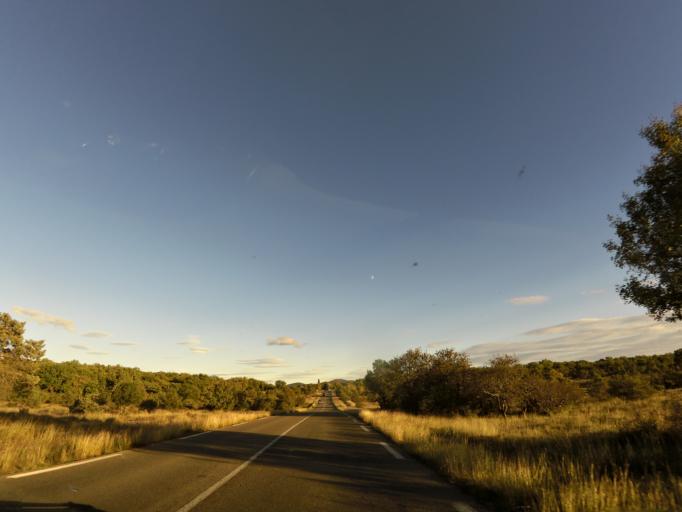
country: FR
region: Languedoc-Roussillon
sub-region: Departement du Gard
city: Saint-Hippolyte-du-Fort
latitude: 43.9506
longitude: 3.8827
